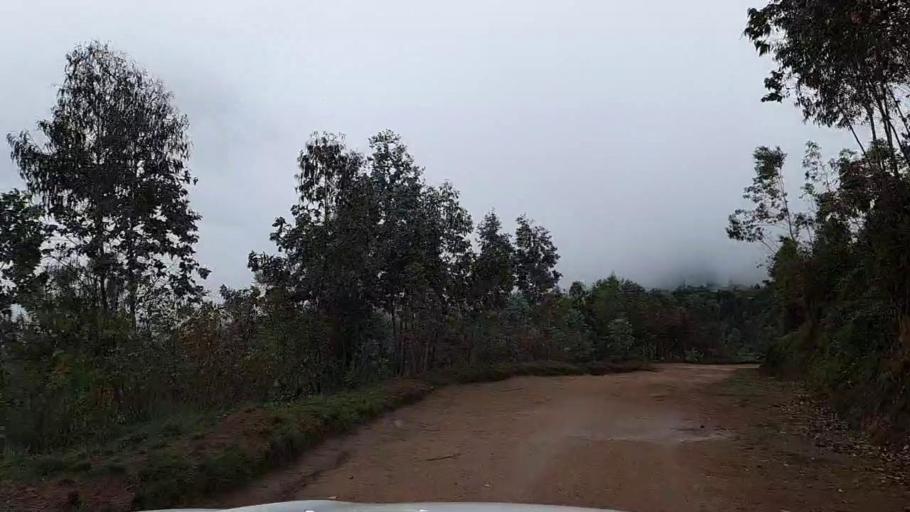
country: RW
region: Southern Province
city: Nzega
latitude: -2.4045
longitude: 29.4940
